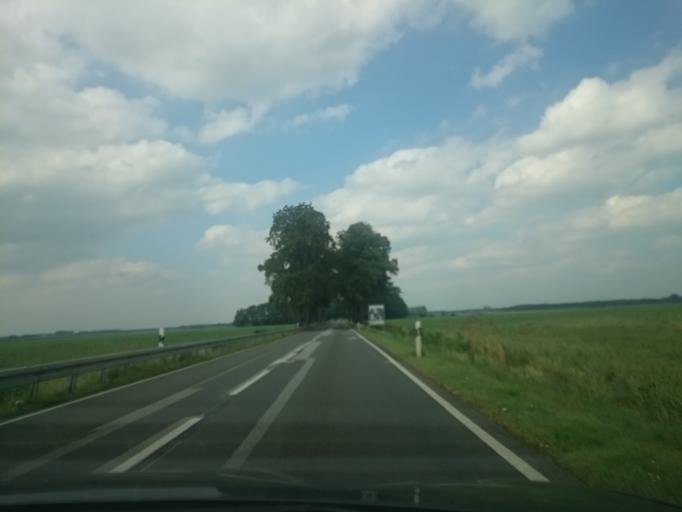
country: DE
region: Mecklenburg-Vorpommern
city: Ferdinandshof
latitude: 53.6714
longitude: 13.8870
